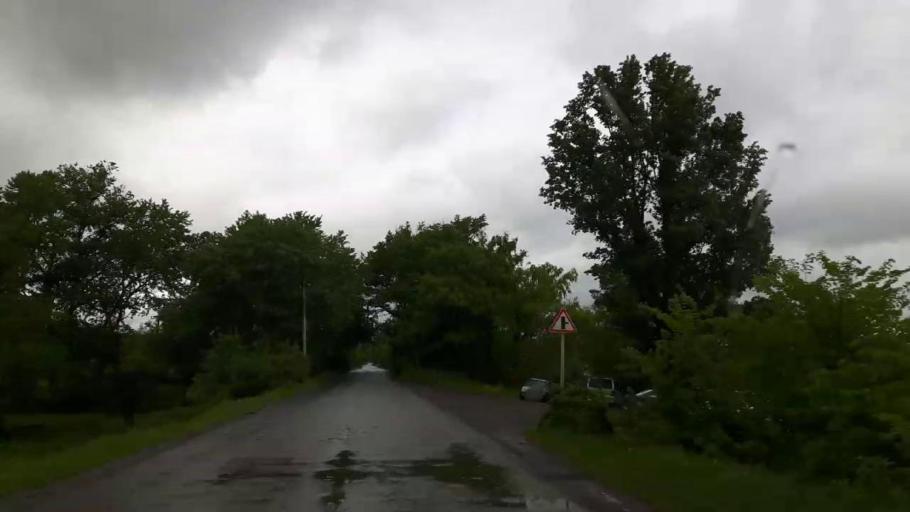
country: GE
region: Shida Kartli
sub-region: Khashuris Raioni
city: Khashuri
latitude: 41.9960
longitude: 43.6559
